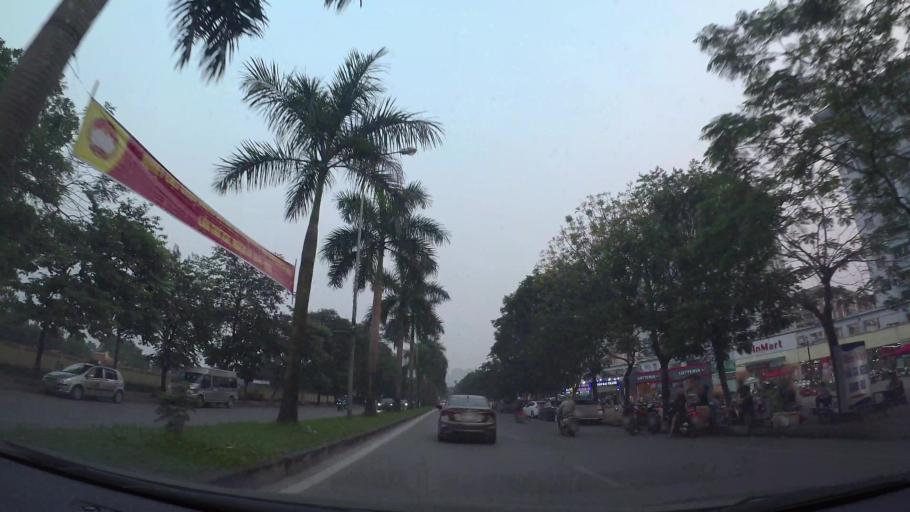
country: VN
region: Ha Noi
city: Ha Dong
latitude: 20.9749
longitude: 105.7896
